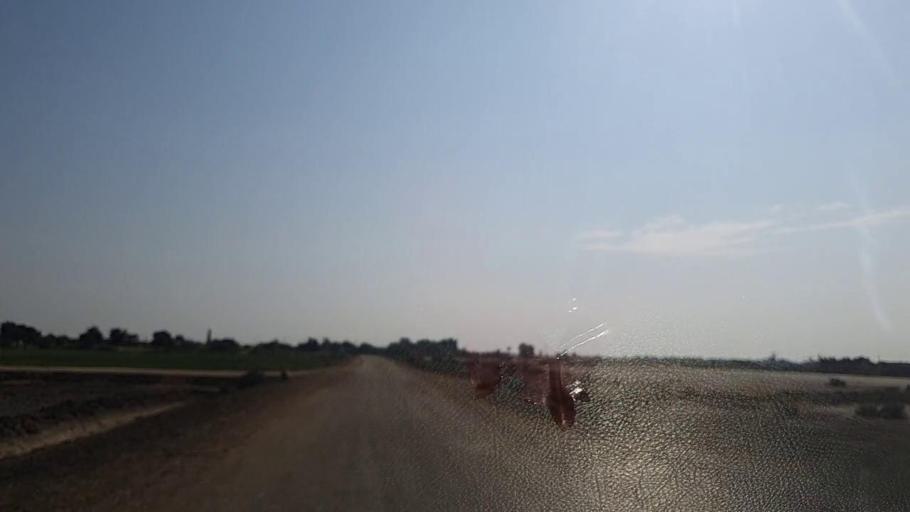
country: PK
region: Sindh
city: Tando Mittha Khan
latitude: 26.0316
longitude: 69.1150
